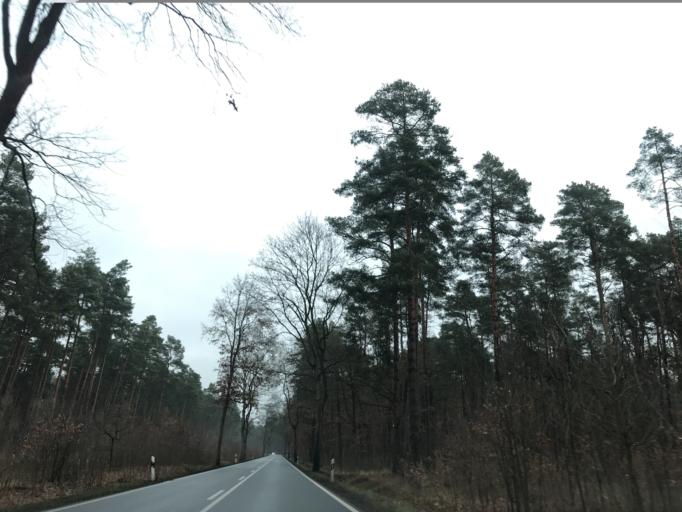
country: DE
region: Brandenburg
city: Kremmen
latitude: 52.7006
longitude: 12.9605
